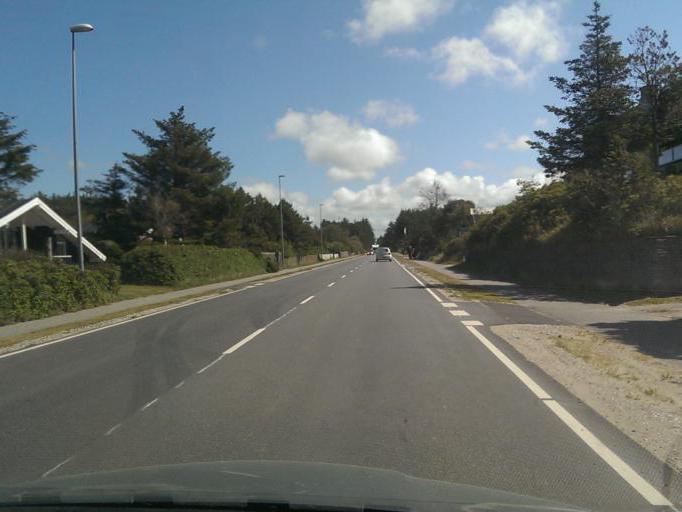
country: DK
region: North Denmark
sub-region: Jammerbugt Kommune
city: Pandrup
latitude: 57.2508
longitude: 9.5935
